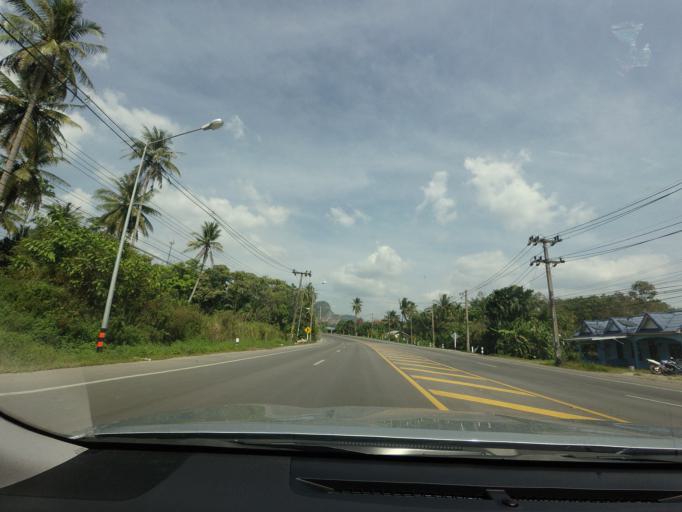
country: TH
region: Phangnga
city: Ban Ao Nang
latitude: 8.0572
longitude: 98.7802
